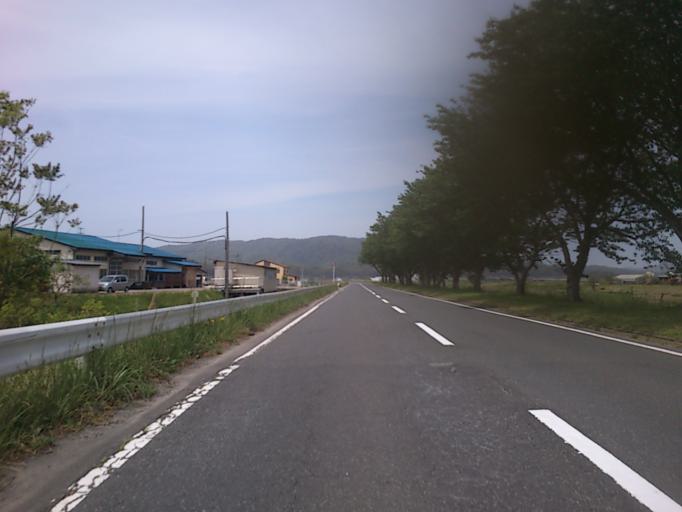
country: JP
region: Kyoto
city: Miyazu
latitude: 35.6611
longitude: 135.0867
